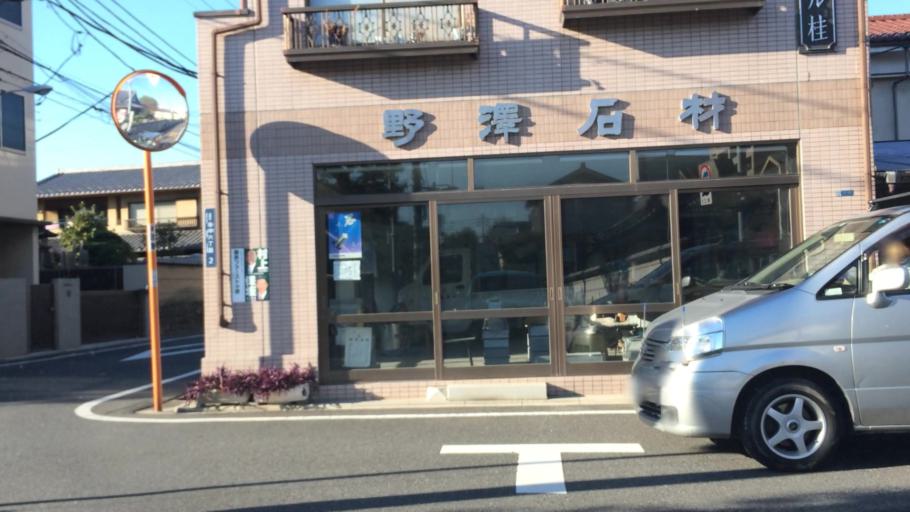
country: JP
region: Tokyo
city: Tokyo
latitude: 35.7214
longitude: 139.7691
